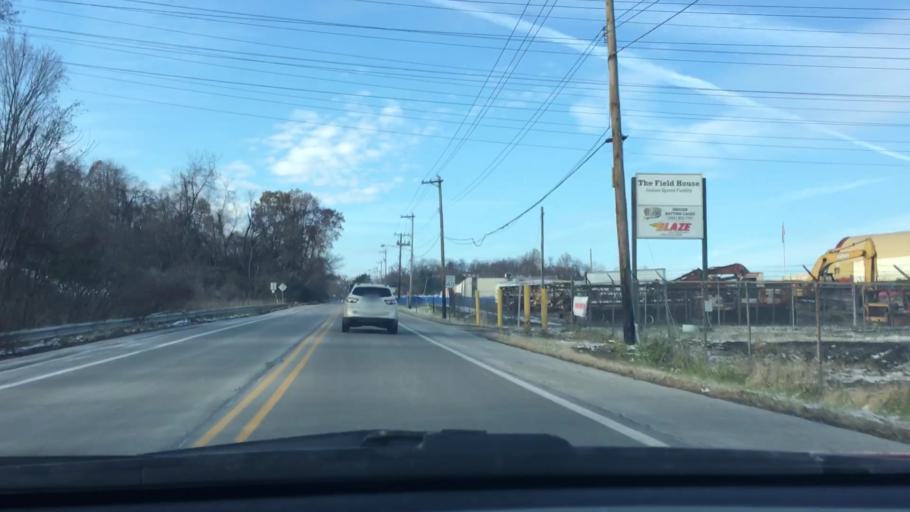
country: US
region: Pennsylvania
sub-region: Allegheny County
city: Glassport
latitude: 40.3379
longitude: -79.9120
